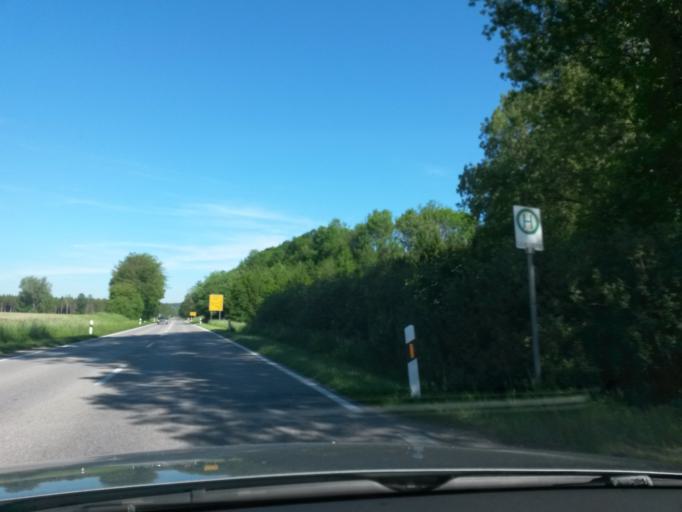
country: DE
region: Baden-Wuerttemberg
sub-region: Tuebingen Region
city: Durnau
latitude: 48.0652
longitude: 9.5777
